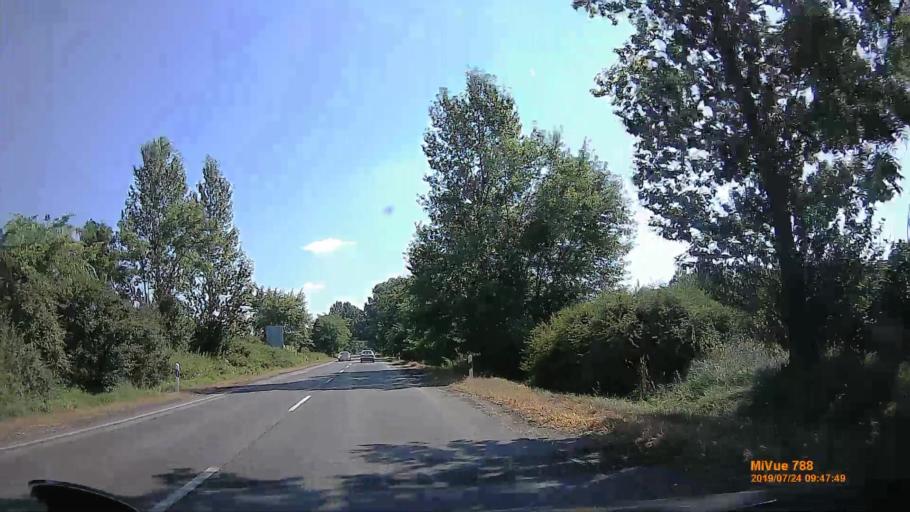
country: HU
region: Szabolcs-Szatmar-Bereg
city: Baktaloranthaza
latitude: 47.9989
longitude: 22.1051
